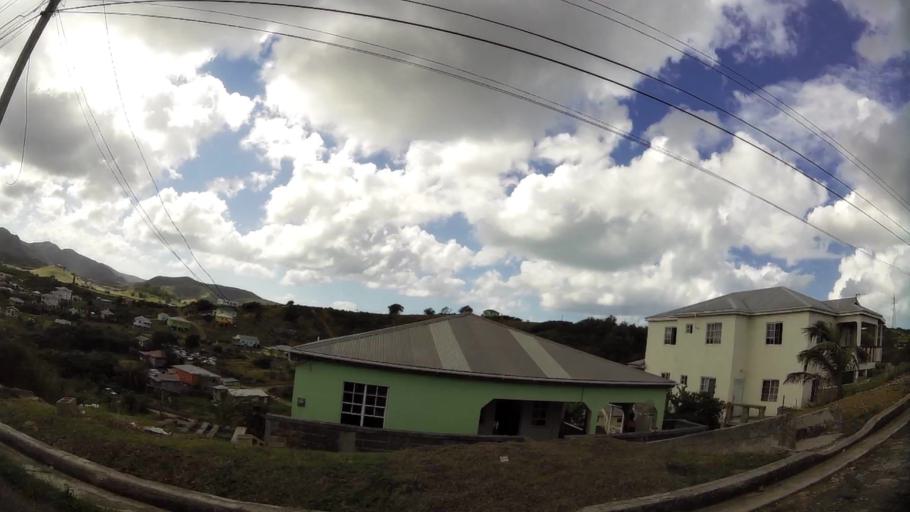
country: AG
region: Saint John
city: Saint John's
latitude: 17.1069
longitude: -61.8539
